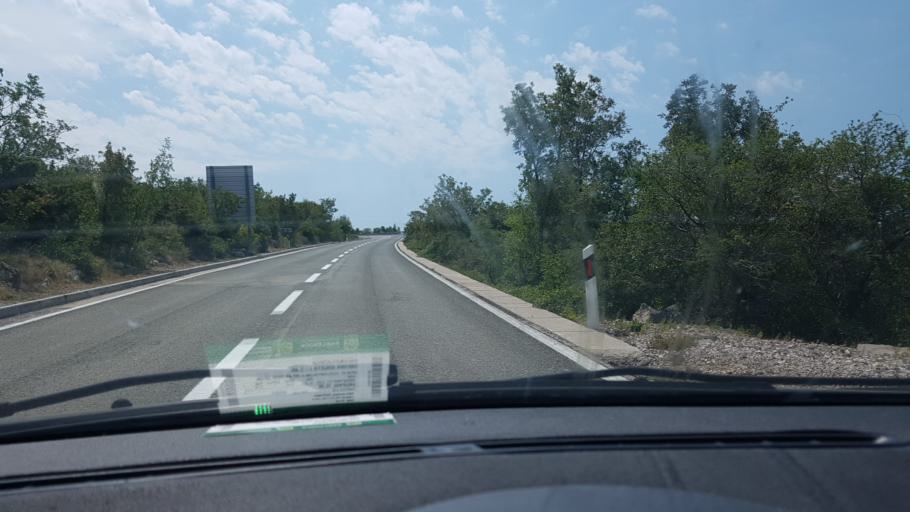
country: HR
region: Primorsko-Goranska
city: Banjol
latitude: 44.7135
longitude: 14.9057
